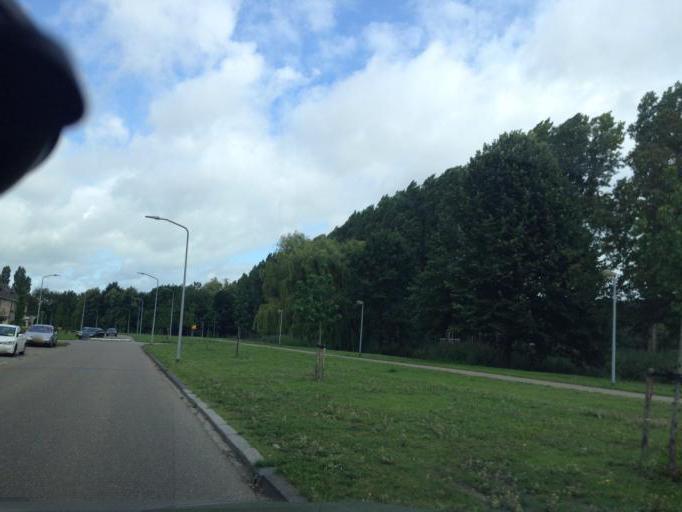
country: NL
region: Flevoland
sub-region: Gemeente Almere
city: Almere Stad
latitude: 52.3716
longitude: 5.1924
